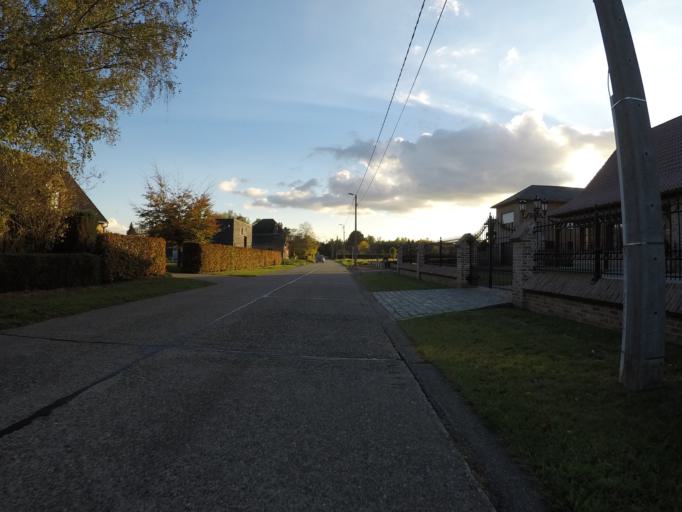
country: BE
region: Flanders
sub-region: Provincie Vlaams-Brabant
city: Begijnendijk
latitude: 50.9994
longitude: 4.8042
